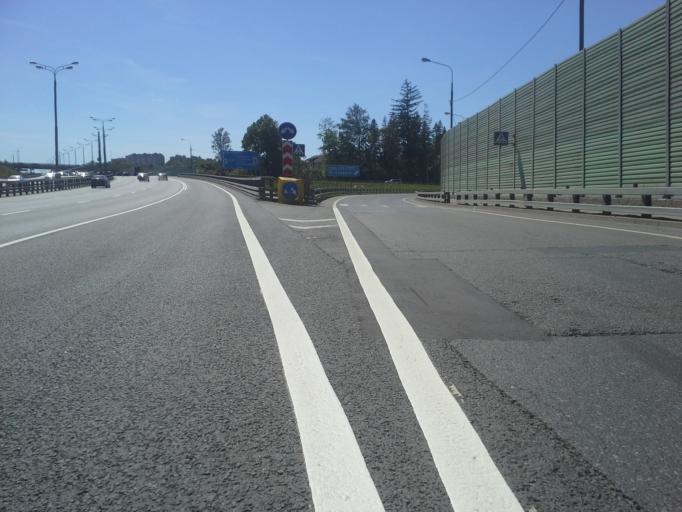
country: RU
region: Moskovskaya
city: Selyatino
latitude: 55.5195
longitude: 37.0004
